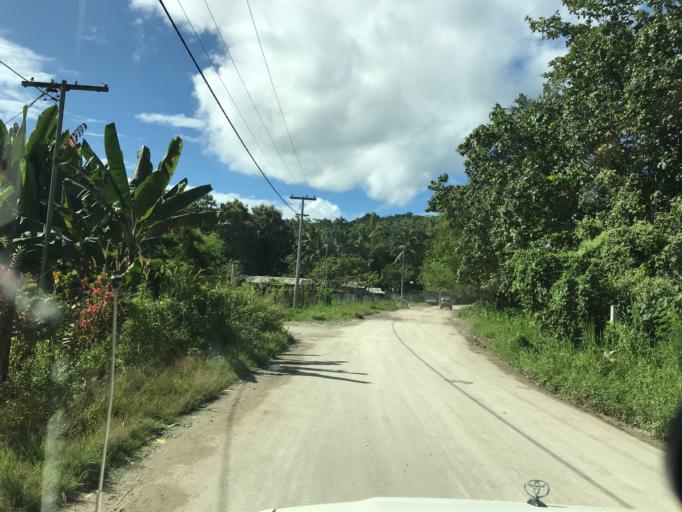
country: SB
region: Malaita
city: Auki
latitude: -8.7721
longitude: 160.7027
